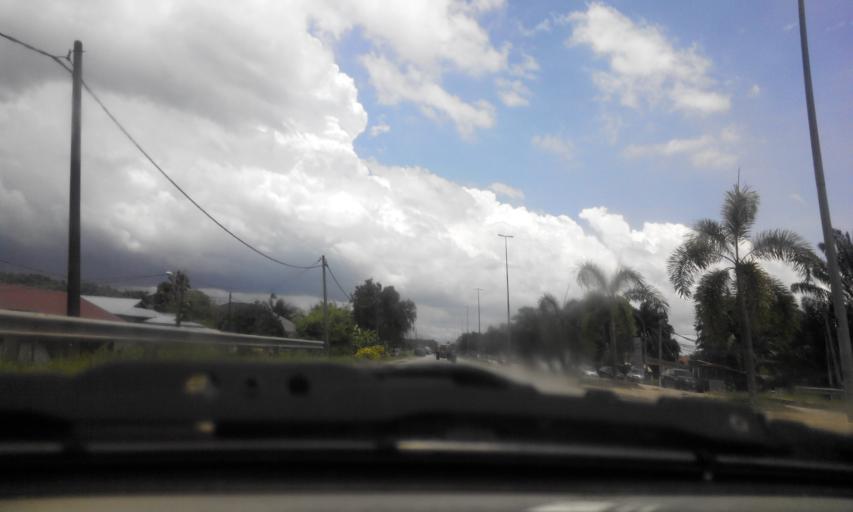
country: MY
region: Perak
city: Parit Buntar
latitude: 5.1184
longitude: 100.5233
